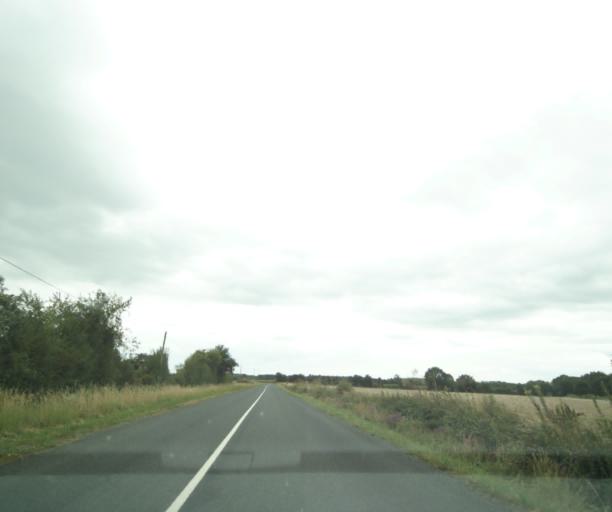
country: FR
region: Pays de la Loire
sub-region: Departement de la Sarthe
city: Precigne
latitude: 47.7527
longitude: -0.3039
